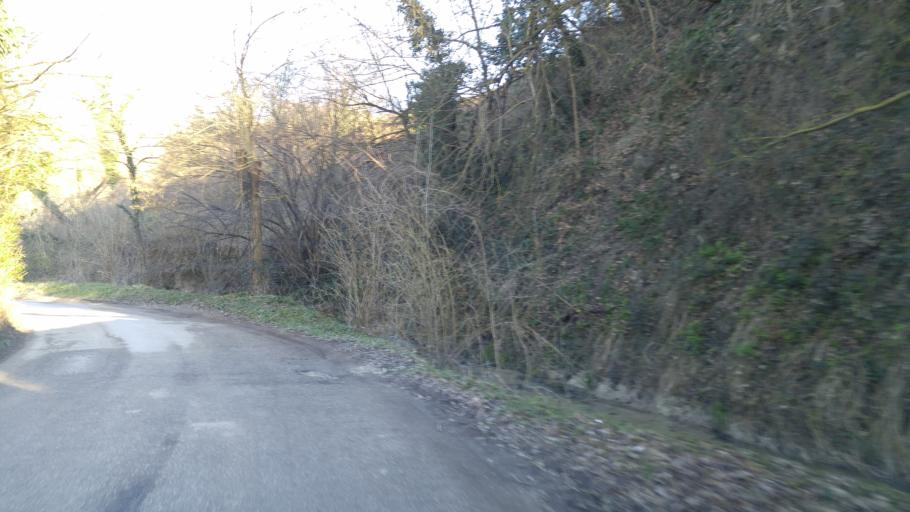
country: IT
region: The Marches
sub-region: Provincia di Pesaro e Urbino
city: Cagli
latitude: 43.5500
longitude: 12.6541
